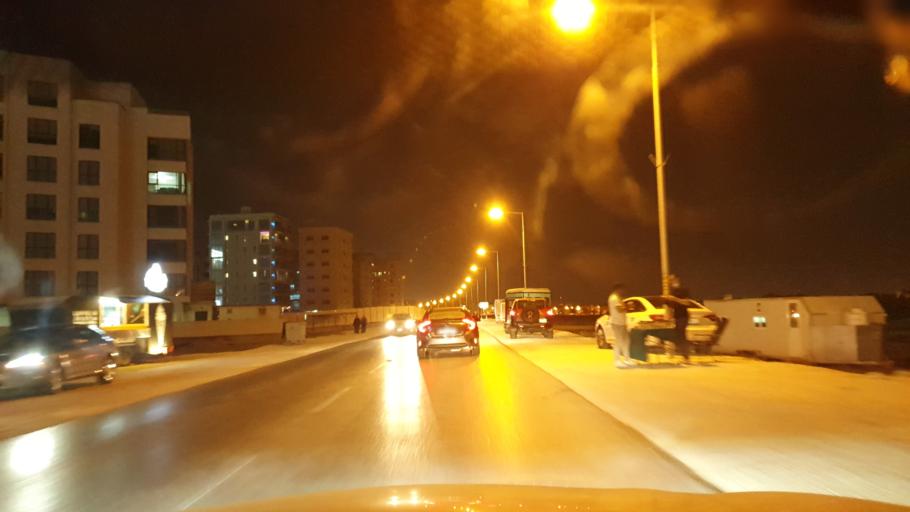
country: BH
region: Northern
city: Madinat `Isa
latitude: 26.1819
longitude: 50.4815
